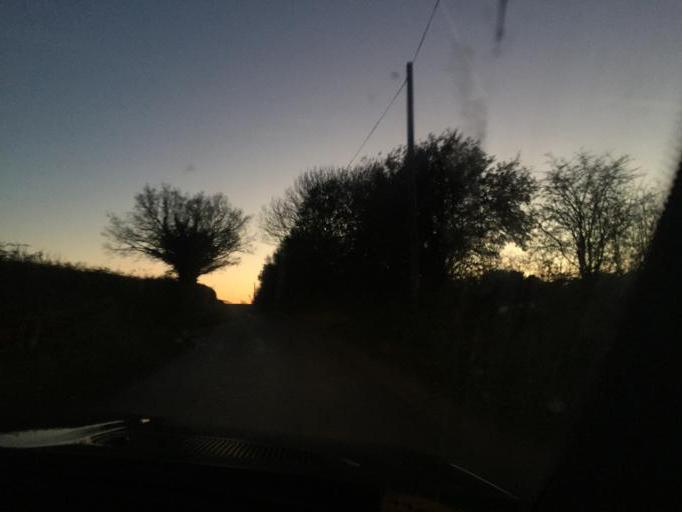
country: GB
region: England
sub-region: Northamptonshire
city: Silverstone
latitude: 52.0769
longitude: -1.0772
